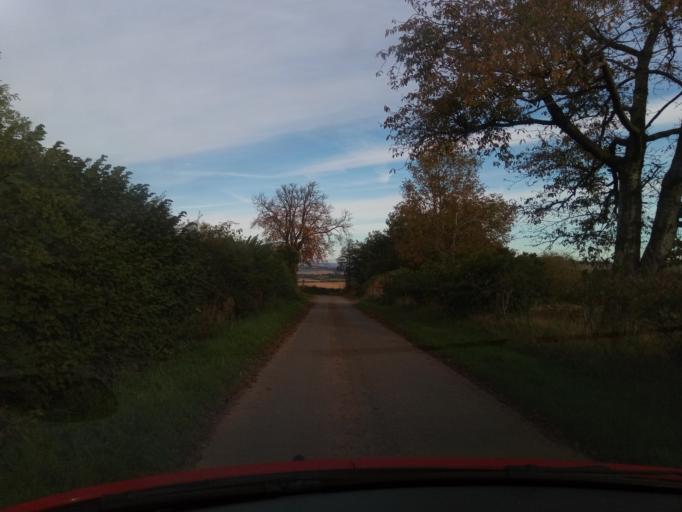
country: GB
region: Scotland
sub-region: The Scottish Borders
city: Jedburgh
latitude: 55.4853
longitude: -2.4984
